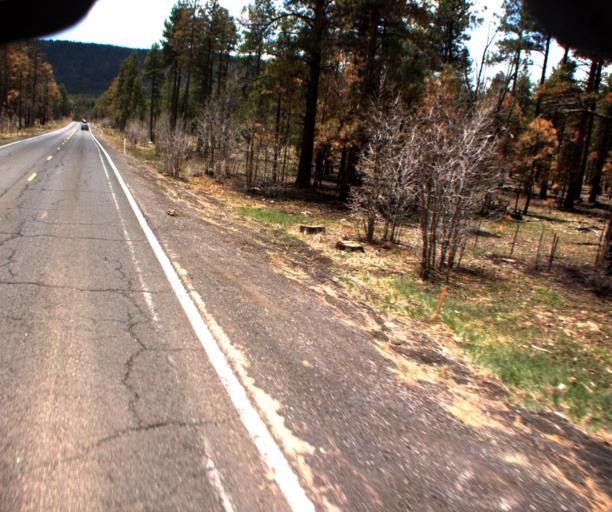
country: US
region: Arizona
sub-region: Coconino County
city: Kachina Village
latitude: 35.1038
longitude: -111.7274
